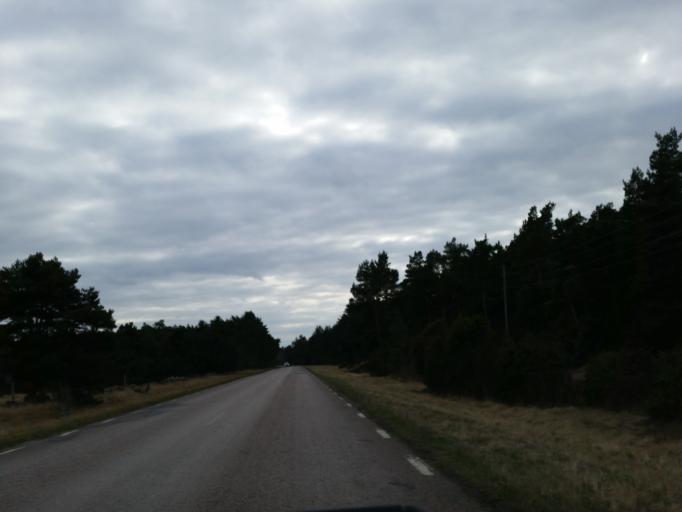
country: SE
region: Kalmar
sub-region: Morbylanga Kommun
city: Sodra Sandby
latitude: 56.5842
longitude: 16.6239
